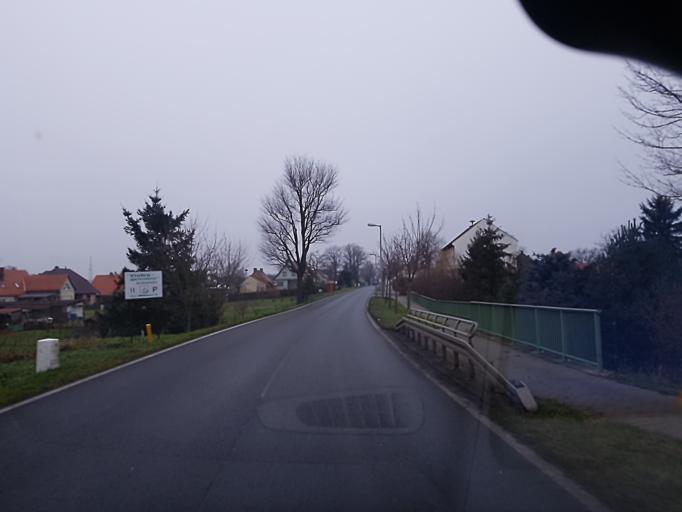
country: DE
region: Brandenburg
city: Lubbenau
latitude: 51.8671
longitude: 13.9195
